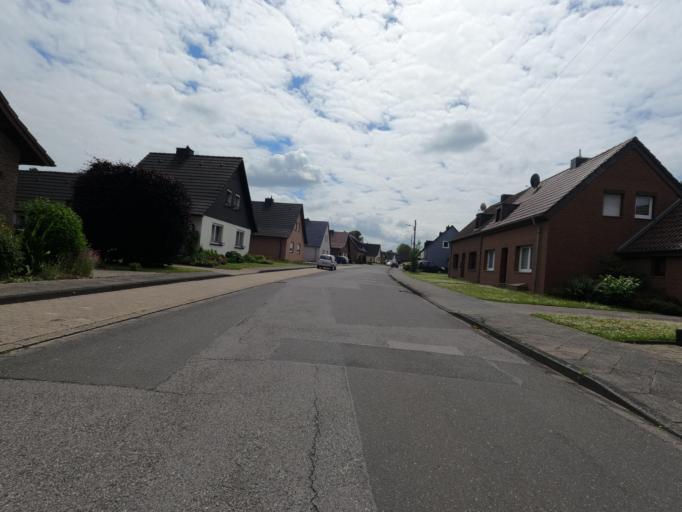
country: DE
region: North Rhine-Westphalia
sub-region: Regierungsbezirk Koln
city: Ubach-Palenberg
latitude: 50.9108
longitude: 6.1473
